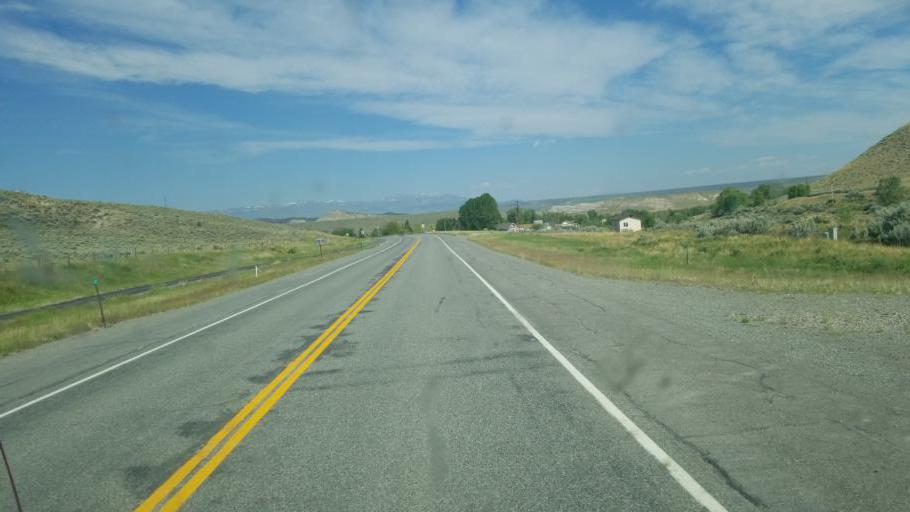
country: US
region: Wyoming
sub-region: Park County
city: Cody
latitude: 44.1542
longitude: -108.8630
